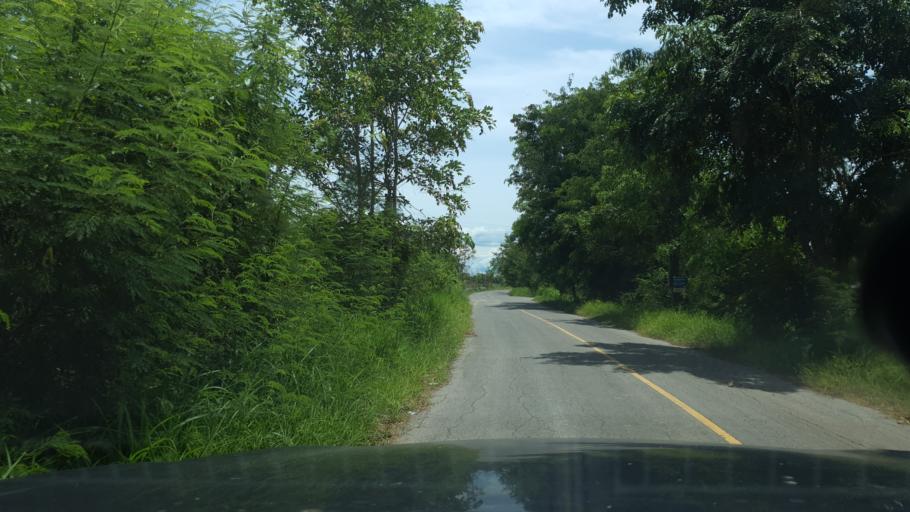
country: TH
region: Sukhothai
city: Ban Na
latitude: 17.0975
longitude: 99.6797
